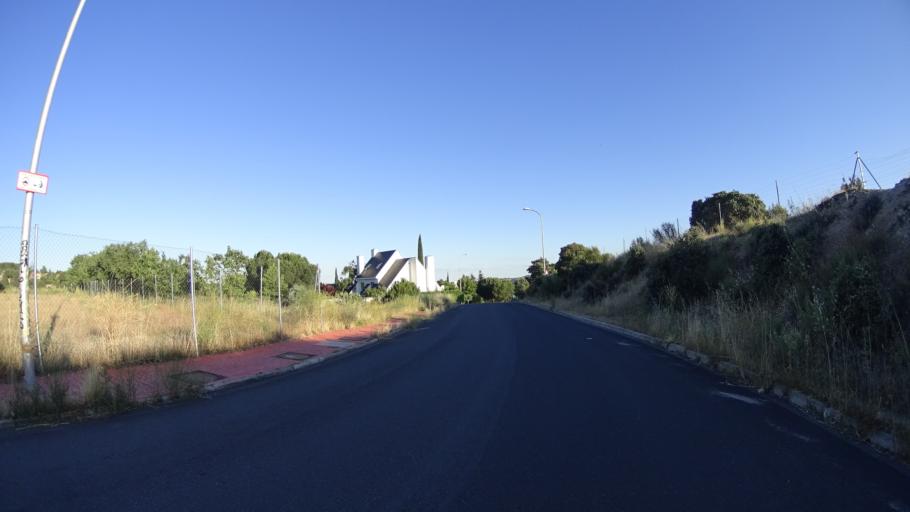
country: ES
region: Madrid
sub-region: Provincia de Madrid
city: Galapagar
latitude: 40.5954
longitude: -3.9733
